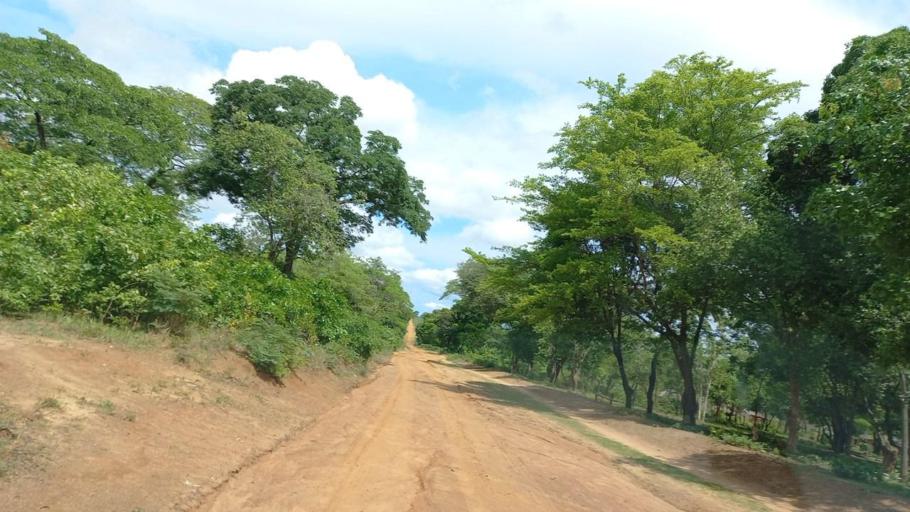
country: ZM
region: North-Western
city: Kabompo
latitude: -13.5441
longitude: 24.1021
